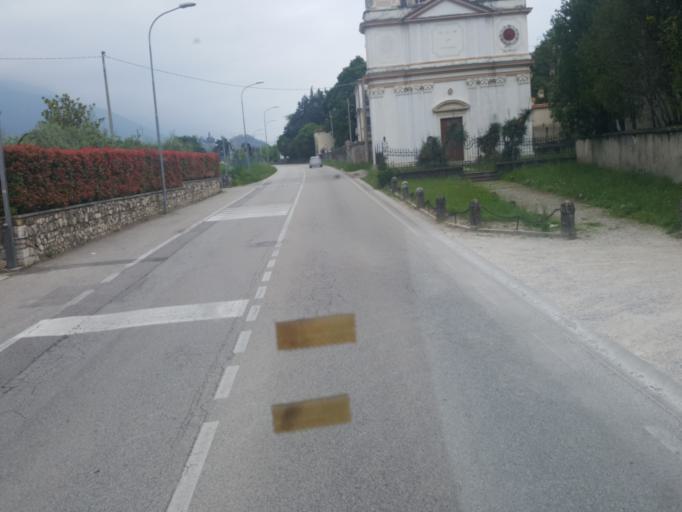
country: IT
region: Veneto
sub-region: Provincia di Vicenza
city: Romano d'Ezzelino
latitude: 45.7832
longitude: 11.7498
